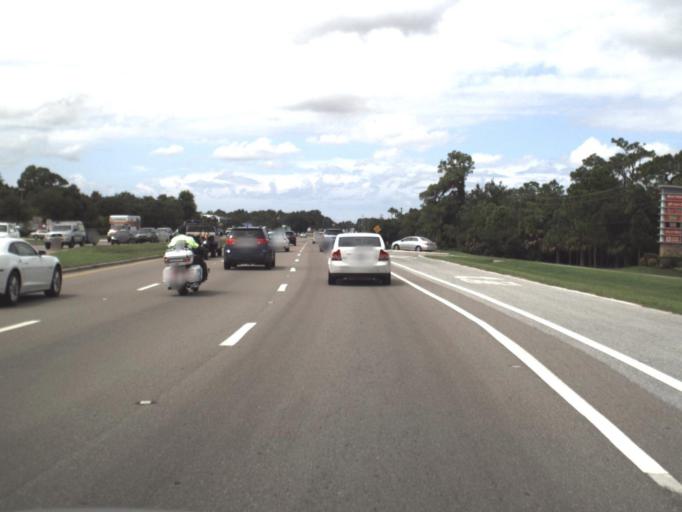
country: US
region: Florida
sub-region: Sarasota County
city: The Meadows
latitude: 27.3888
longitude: -82.4566
